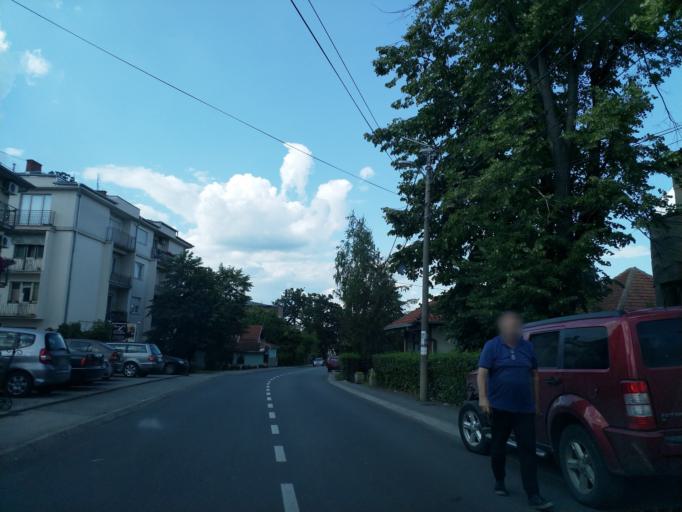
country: RS
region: Central Serbia
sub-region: Raski Okrug
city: Vrnjacka Banja
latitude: 43.6212
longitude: 20.8974
